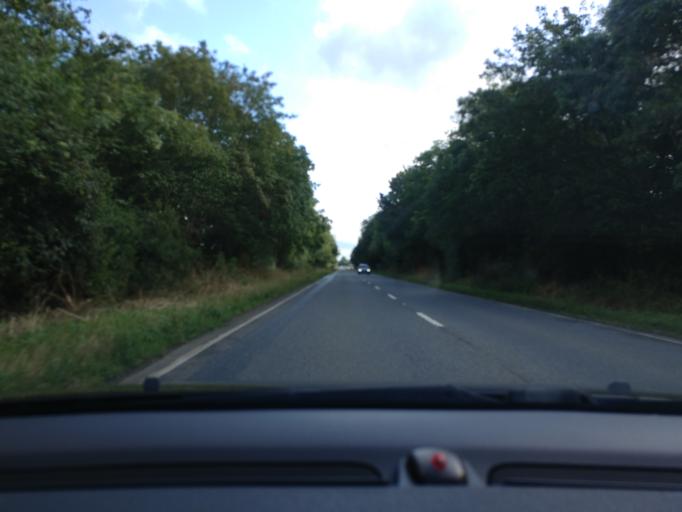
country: GB
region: England
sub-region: Oxfordshire
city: Bicester
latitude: 51.8874
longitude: -1.2275
